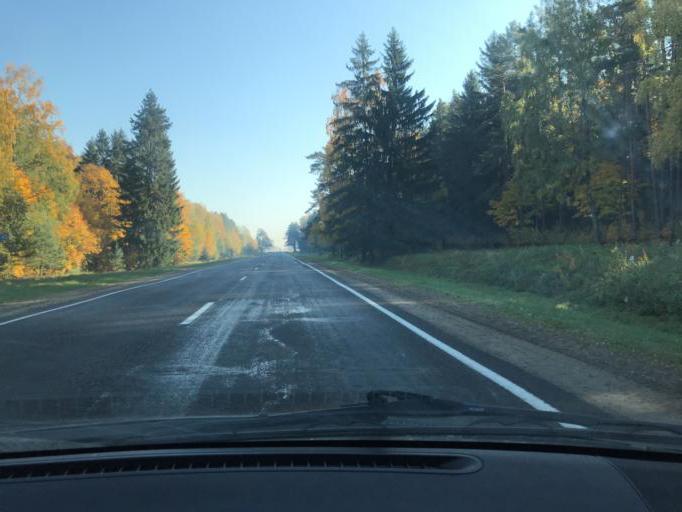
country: BY
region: Minsk
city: Klyetsk
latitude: 52.9696
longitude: 26.6314
